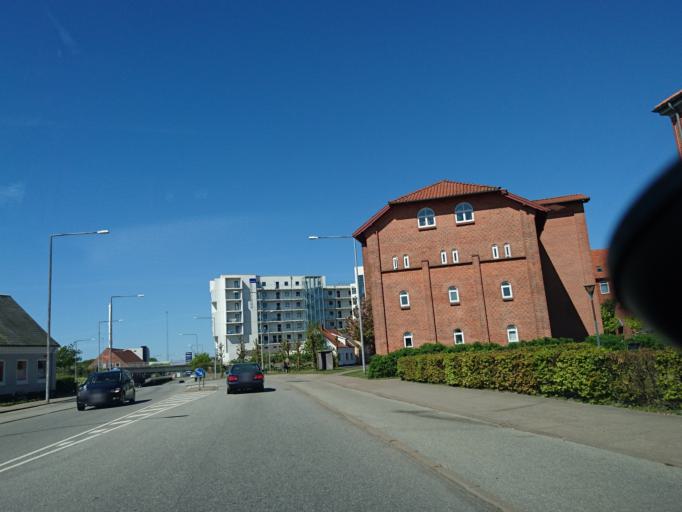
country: DK
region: North Denmark
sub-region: Hjorring Kommune
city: Hjorring
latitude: 57.4561
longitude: 9.9988
